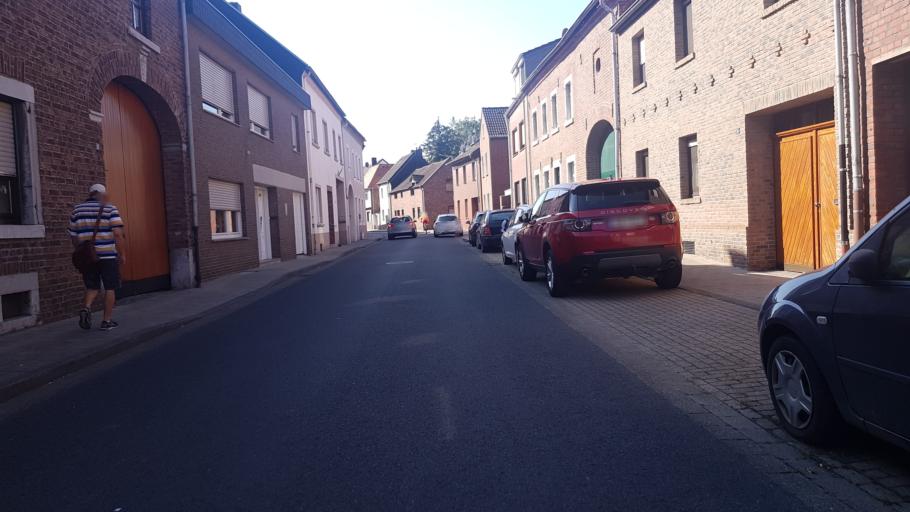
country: DE
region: North Rhine-Westphalia
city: Siersdorf
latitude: 50.8976
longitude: 6.2218
